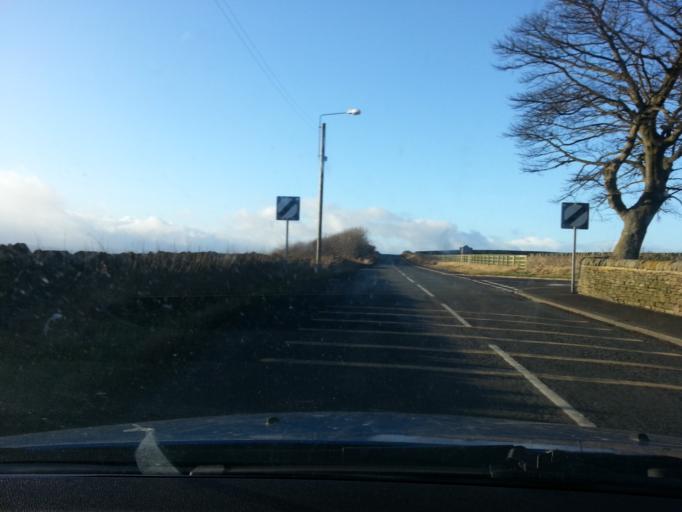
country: GB
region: England
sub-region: County Durham
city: Crook
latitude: 54.7366
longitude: -1.7562
